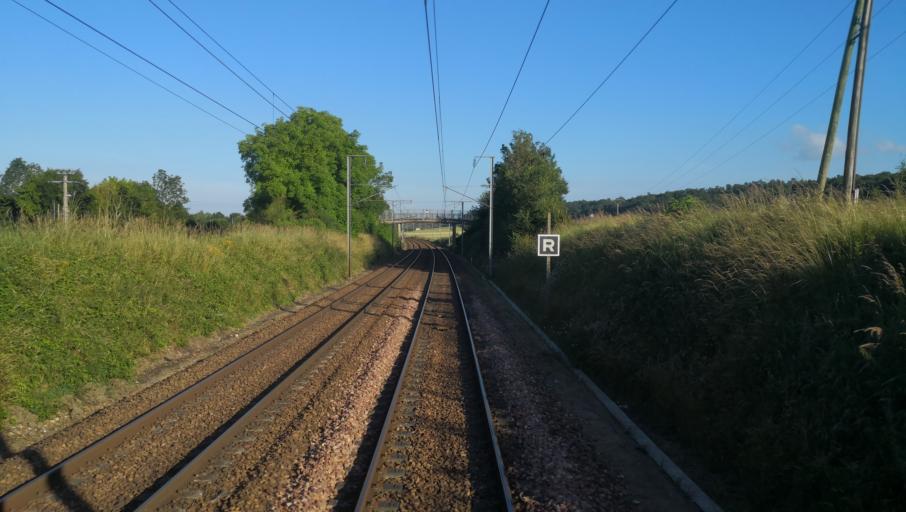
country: FR
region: Haute-Normandie
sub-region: Departement de l'Eure
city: Nassandres
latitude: 49.0919
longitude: 0.7468
